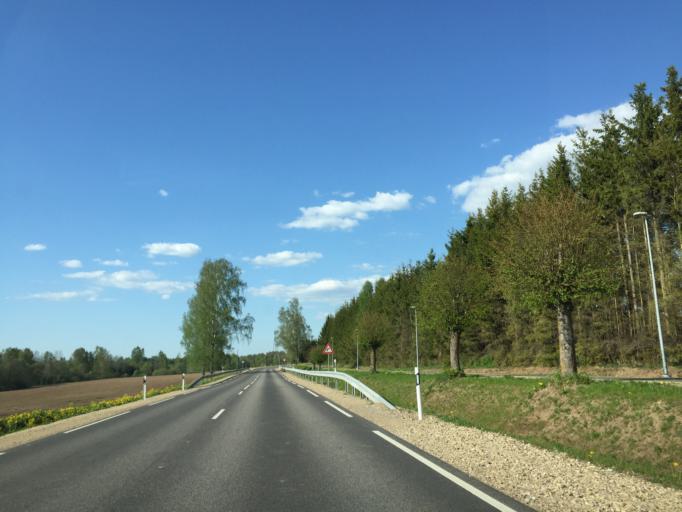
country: LV
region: Limbazu Rajons
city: Limbazi
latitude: 57.4945
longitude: 24.7092
